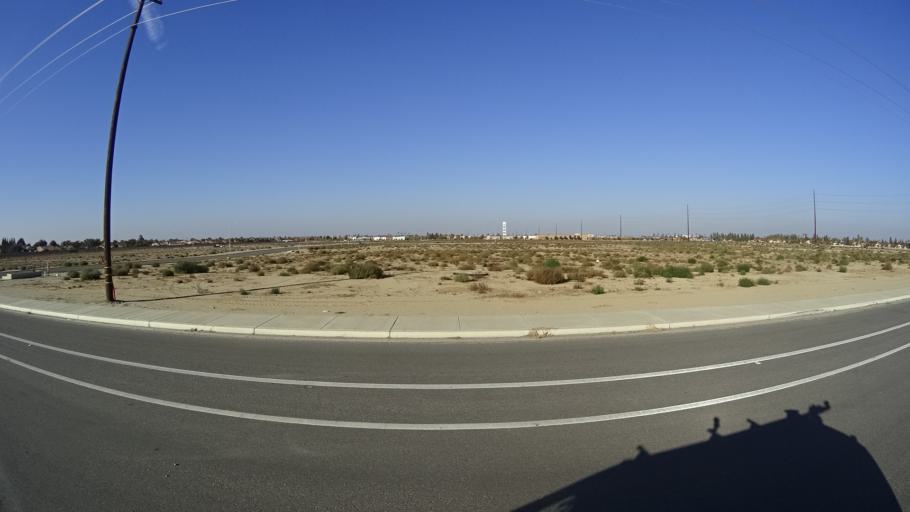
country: US
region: California
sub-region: Kern County
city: Greenacres
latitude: 35.2962
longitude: -119.0982
